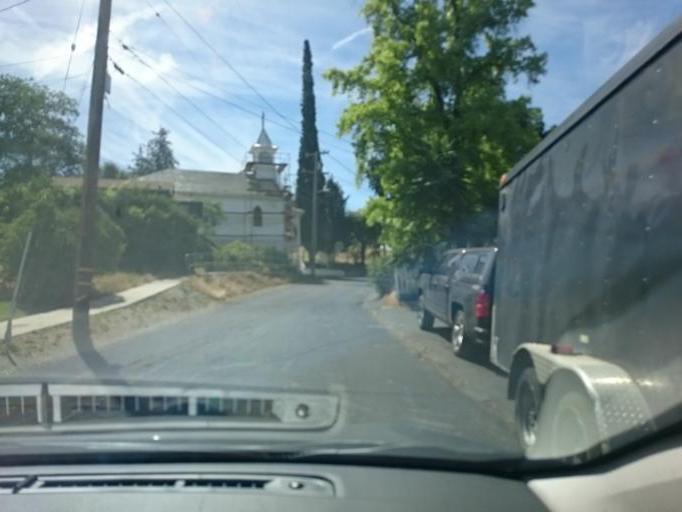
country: US
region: California
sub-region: Tuolumne County
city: Jamestown
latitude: 37.9531
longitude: -120.4225
